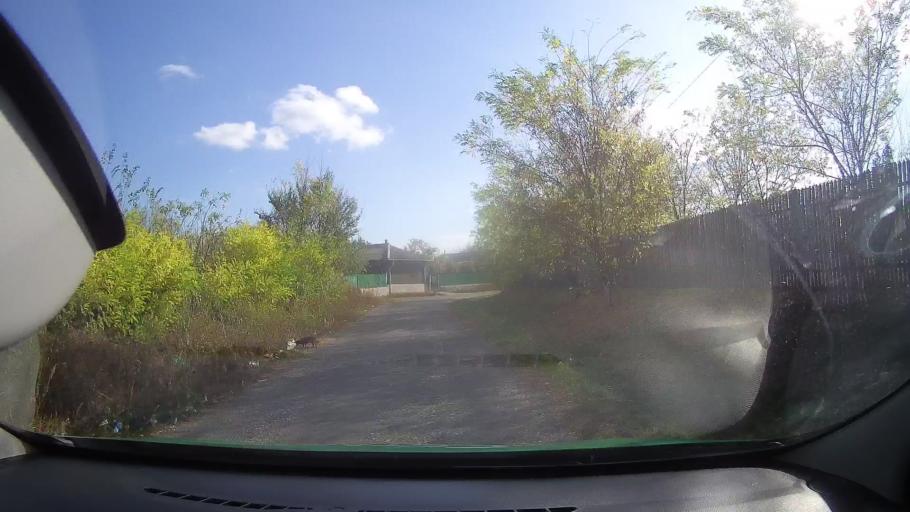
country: RO
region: Constanta
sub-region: Comuna Istria
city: Istria
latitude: 44.5730
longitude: 28.7144
